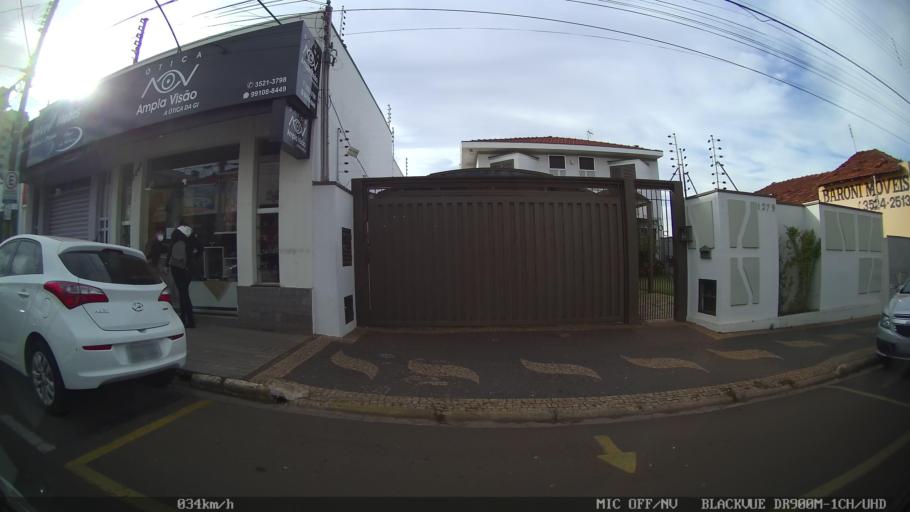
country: BR
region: Sao Paulo
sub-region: Catanduva
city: Catanduva
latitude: -21.1417
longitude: -48.9744
